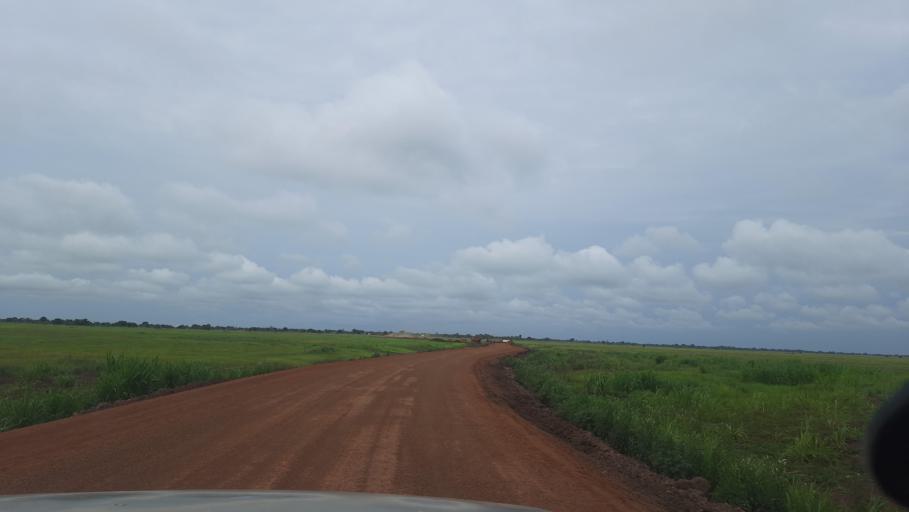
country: ET
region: Gambela
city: Gambela
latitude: 8.3413
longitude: 33.7791
